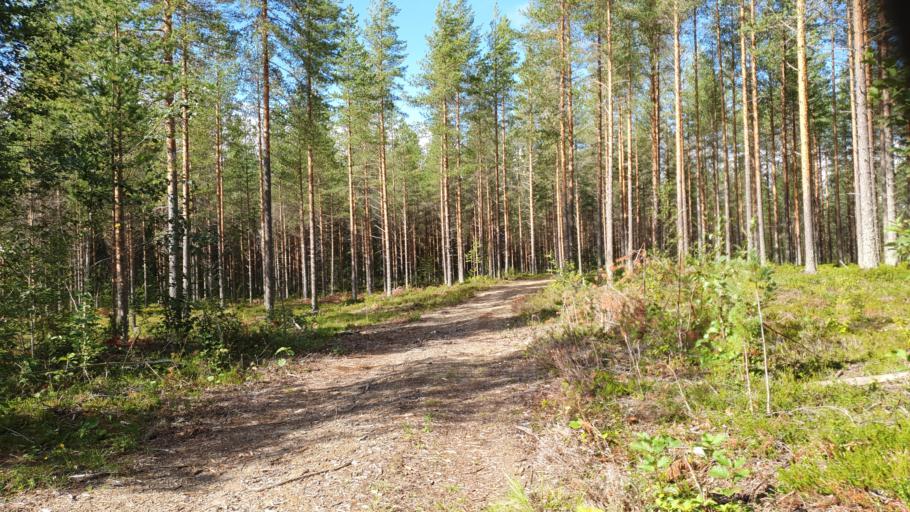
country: FI
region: Kainuu
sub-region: Kehys-Kainuu
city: Kuhmo
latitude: 64.1464
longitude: 29.3435
